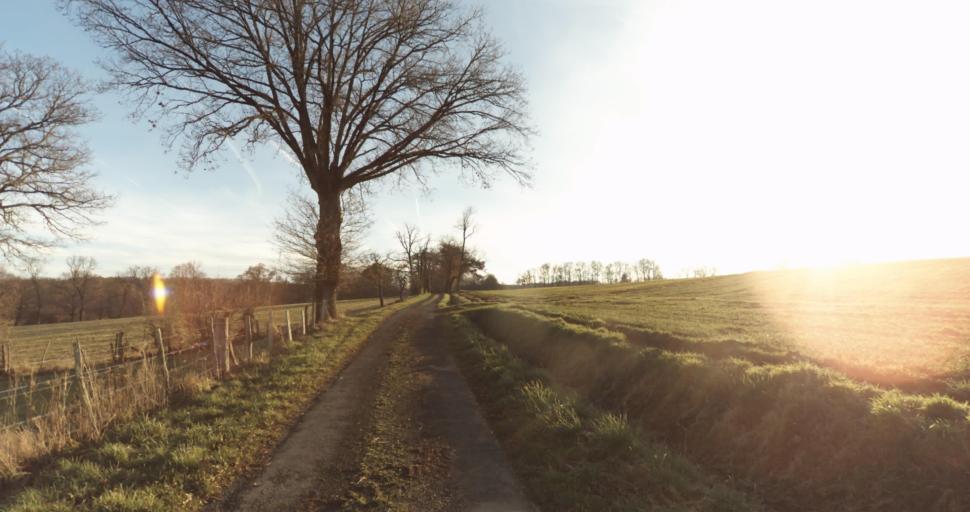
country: FR
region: Limousin
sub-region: Departement de la Haute-Vienne
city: Aixe-sur-Vienne
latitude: 45.7821
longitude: 1.1458
